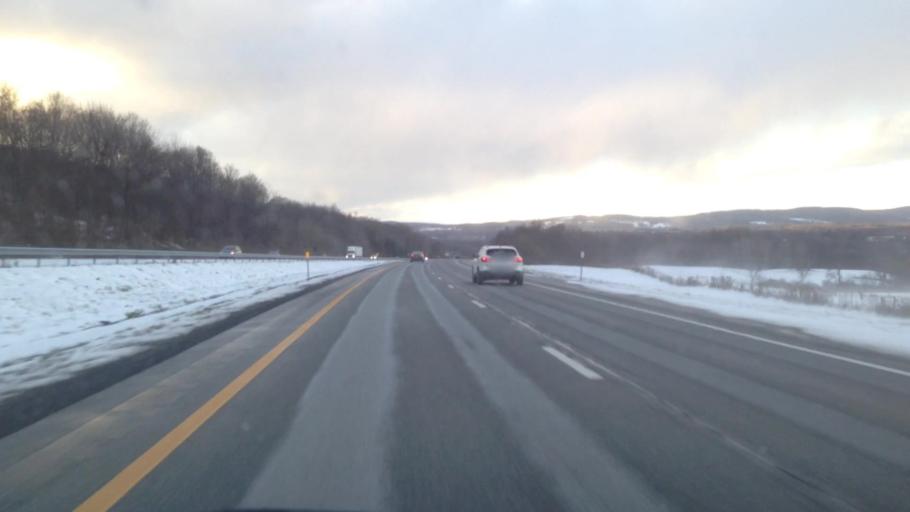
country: US
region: New York
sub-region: Herkimer County
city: Little Falls
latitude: 43.0077
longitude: -74.9041
